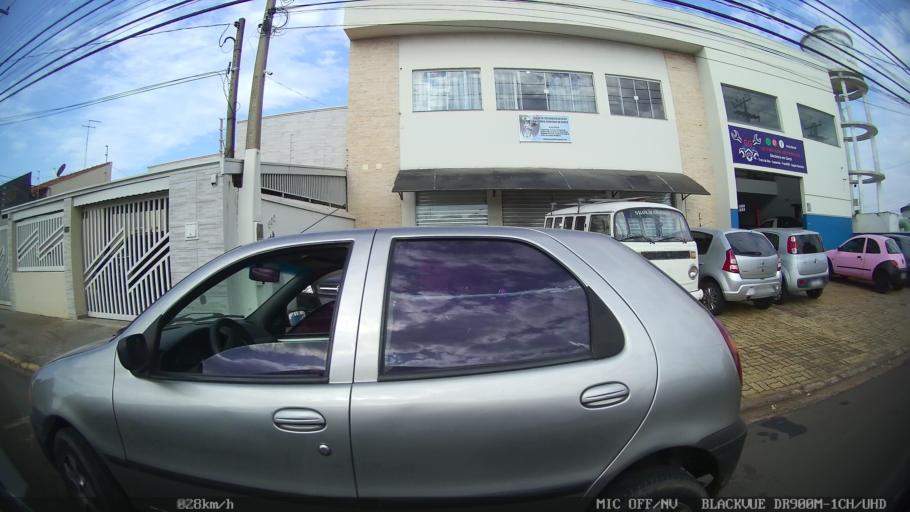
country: BR
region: Sao Paulo
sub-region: Paulinia
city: Paulinia
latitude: -22.7602
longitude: -47.1526
